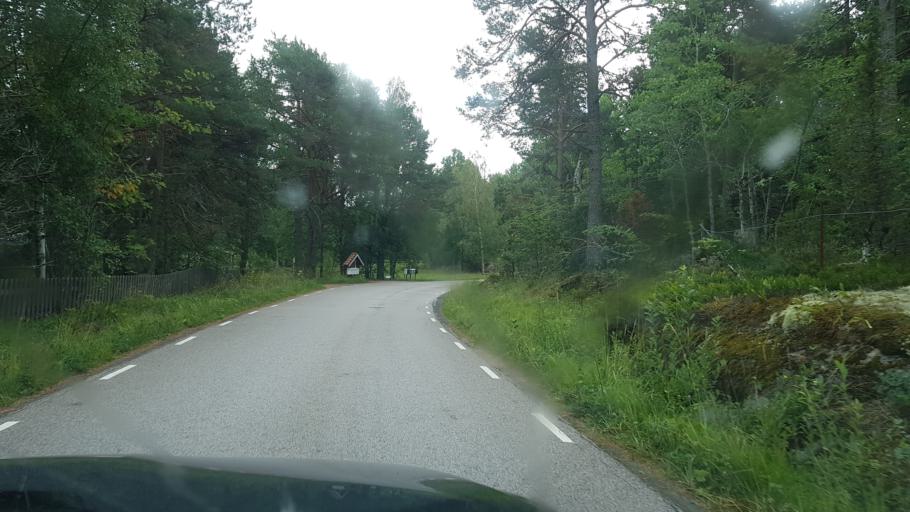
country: SE
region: Uppsala
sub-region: Osthammars Kommun
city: Oregrund
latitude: 60.4004
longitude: 18.4016
